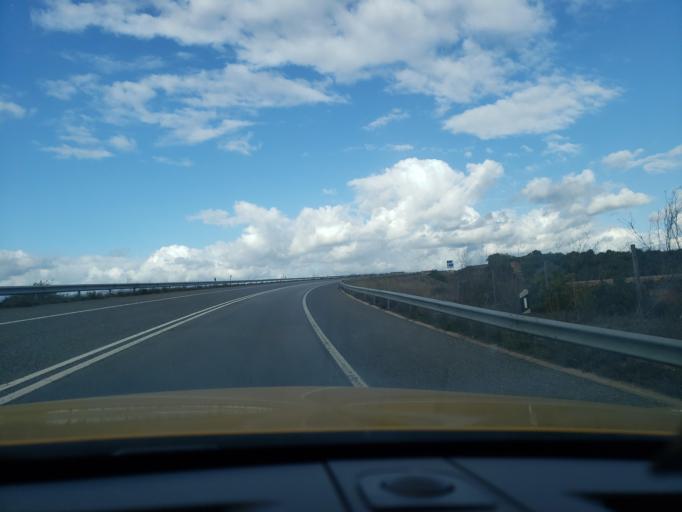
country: PT
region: Faro
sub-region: Portimao
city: Alvor
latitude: 37.1663
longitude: -8.5701
